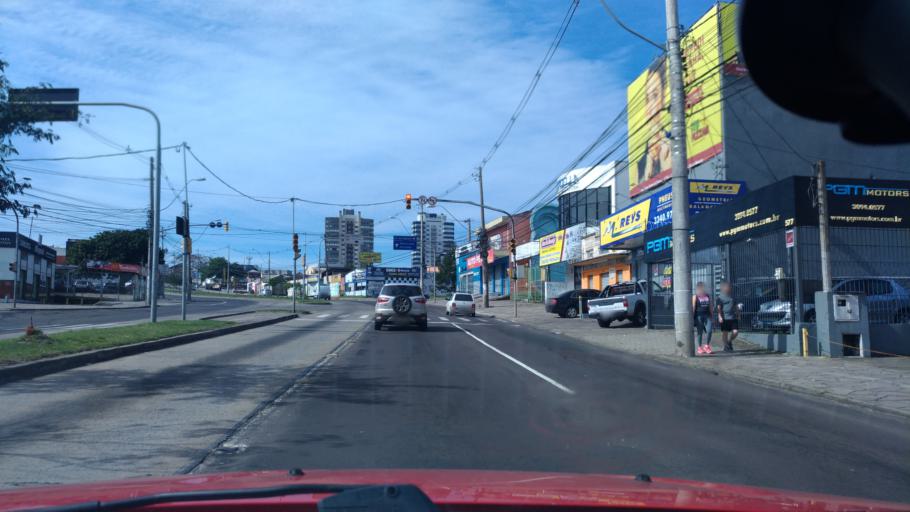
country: BR
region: Rio Grande do Sul
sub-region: Cachoeirinha
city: Cachoeirinha
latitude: -30.0103
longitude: -51.1389
